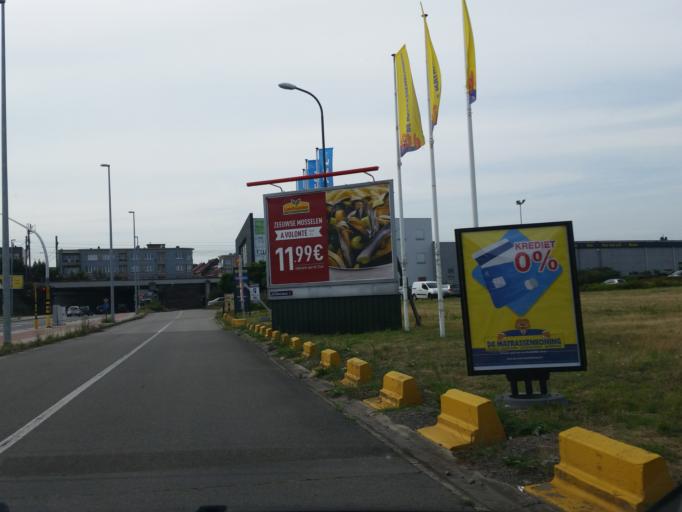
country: BE
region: Flanders
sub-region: Provincie Vlaams-Brabant
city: Vilvoorde
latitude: 50.9257
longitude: 4.4361
